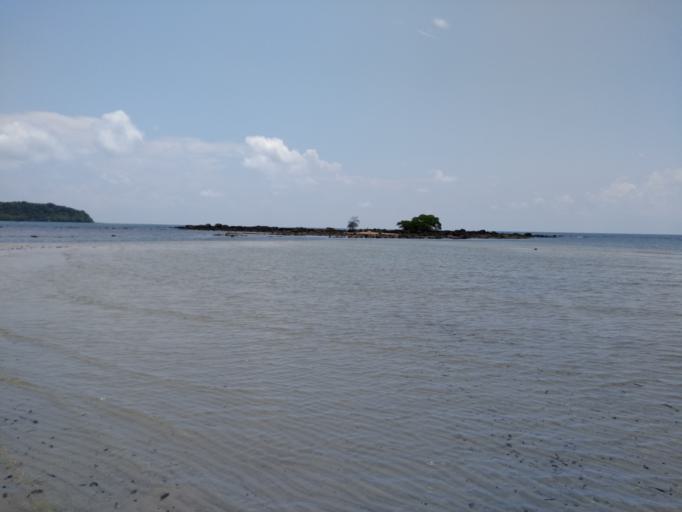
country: TH
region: Trat
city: Ko Kut
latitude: 11.6255
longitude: 102.5445
